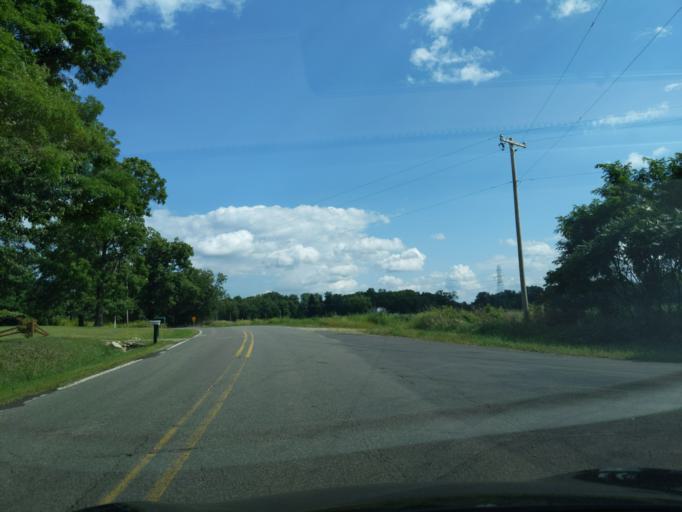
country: US
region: Michigan
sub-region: Jackson County
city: Spring Arbor
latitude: 42.3013
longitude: -84.5068
